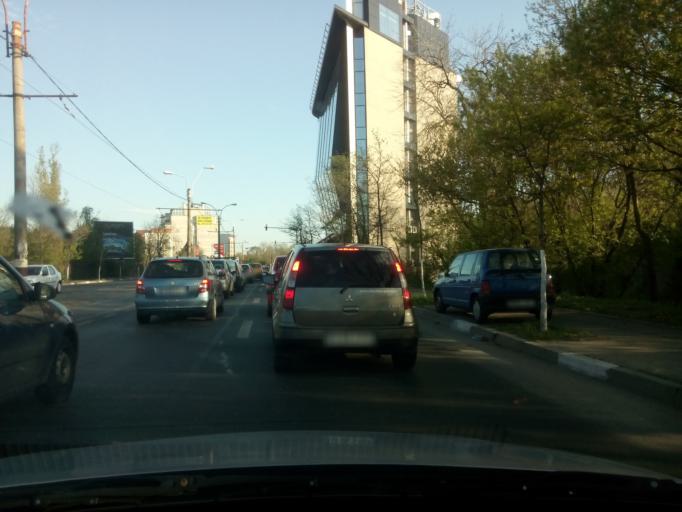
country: RO
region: Bucuresti
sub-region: Municipiul Bucuresti
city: Bucharest
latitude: 44.4716
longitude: 26.1090
